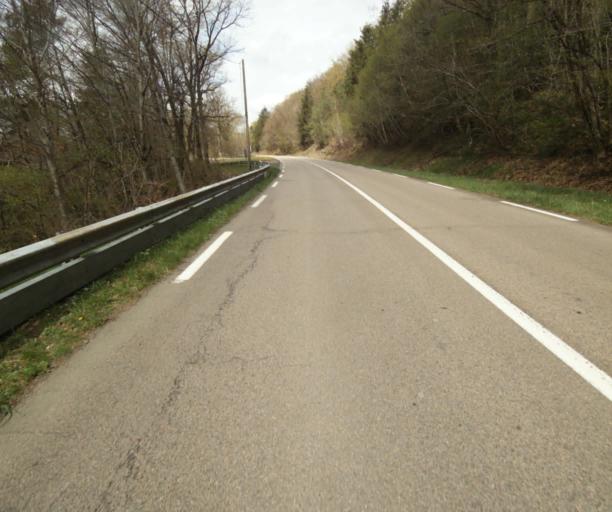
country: FR
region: Limousin
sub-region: Departement de la Correze
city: Sainte-Fortunade
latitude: 45.1955
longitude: 1.8368
